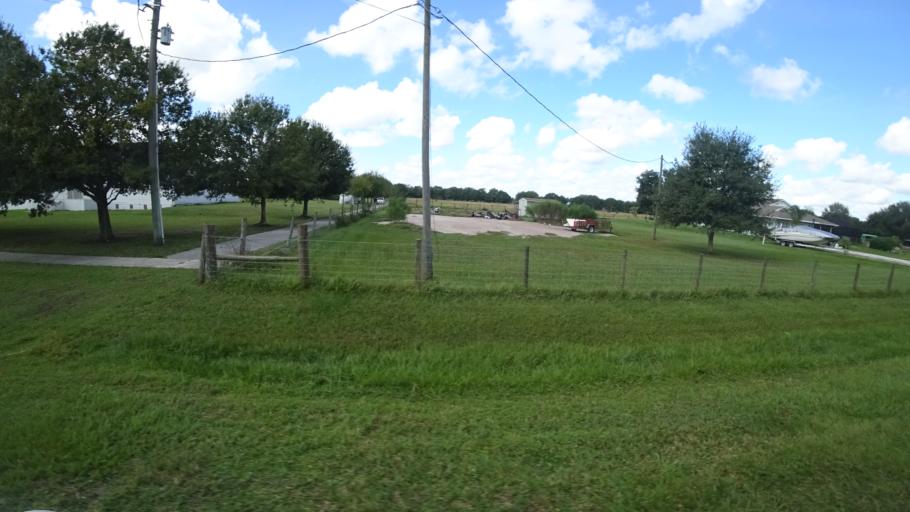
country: US
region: Florida
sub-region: Sarasota County
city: Lake Sarasota
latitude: 27.3596
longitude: -82.1626
